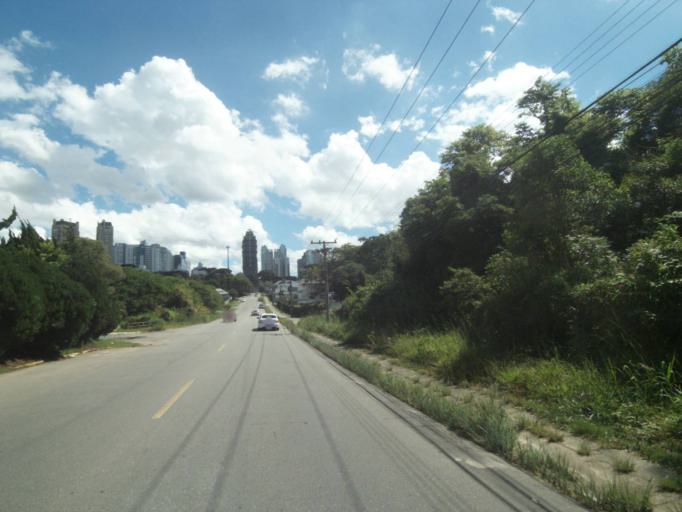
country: BR
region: Parana
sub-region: Curitiba
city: Curitiba
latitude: -25.4324
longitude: -49.3343
